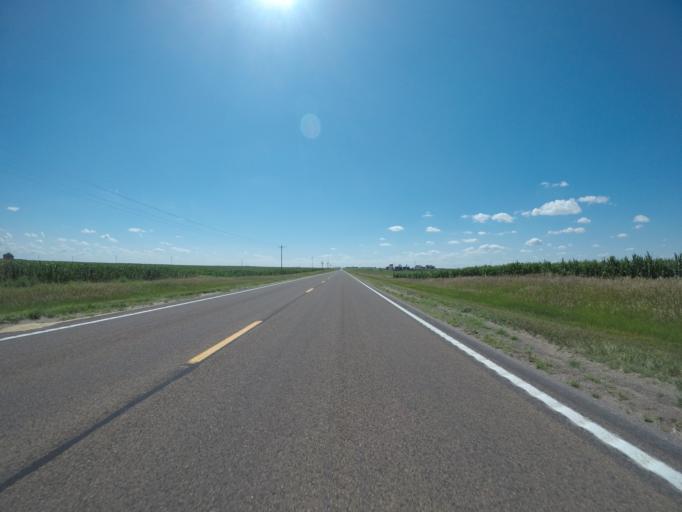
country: US
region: Nebraska
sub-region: Chase County
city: Imperial
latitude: 40.5376
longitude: -101.7377
